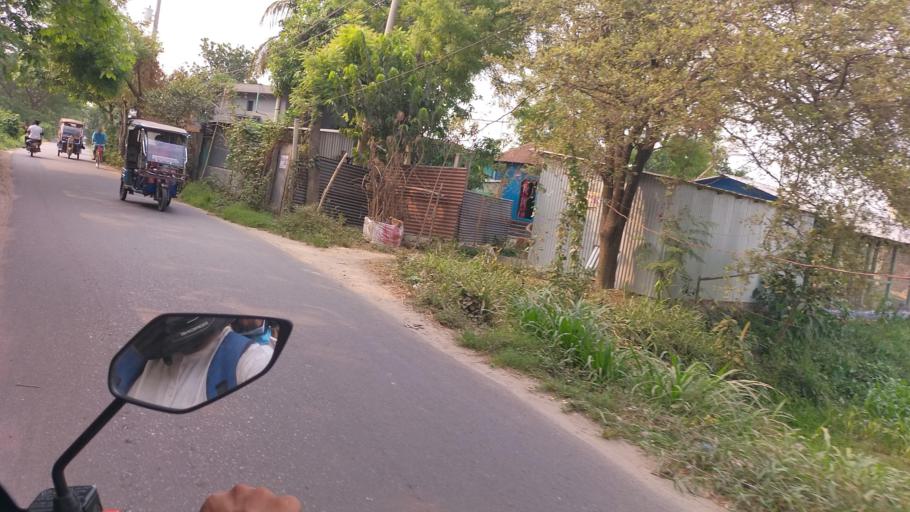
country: BD
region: Dhaka
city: Azimpur
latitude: 23.6680
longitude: 90.3479
